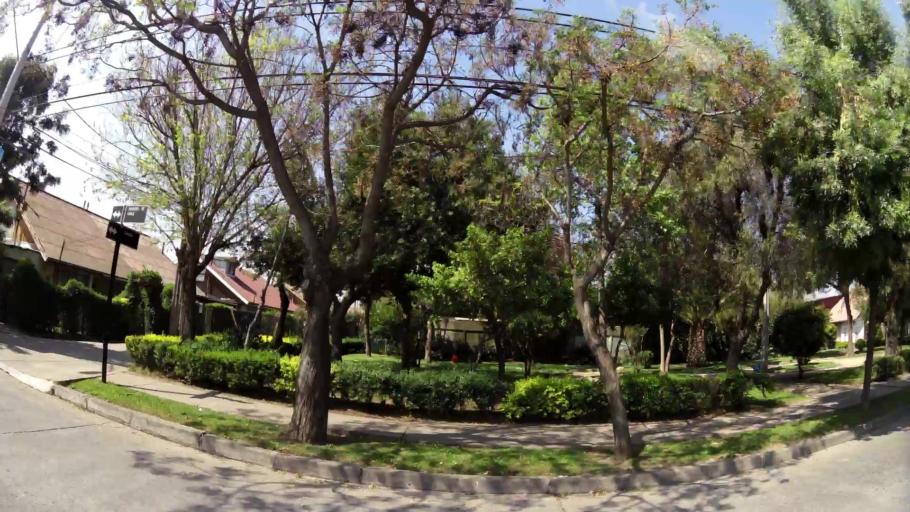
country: CL
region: Santiago Metropolitan
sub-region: Provincia de Santiago
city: La Pintana
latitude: -33.5528
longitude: -70.5993
